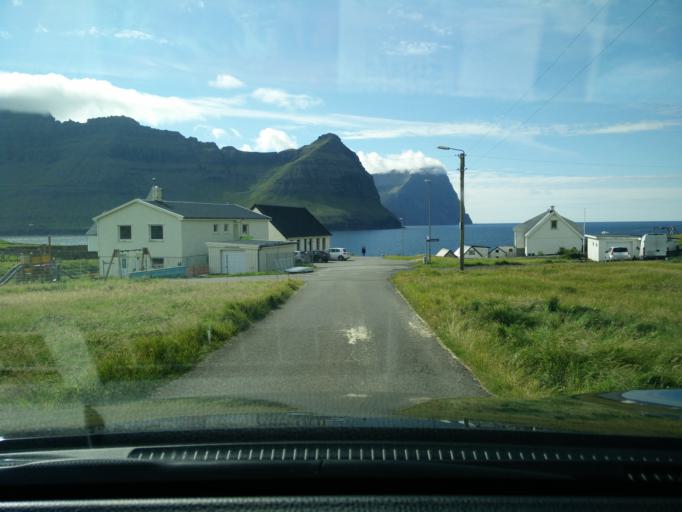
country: FO
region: Nordoyar
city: Klaksvik
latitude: 62.3604
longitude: -6.5414
